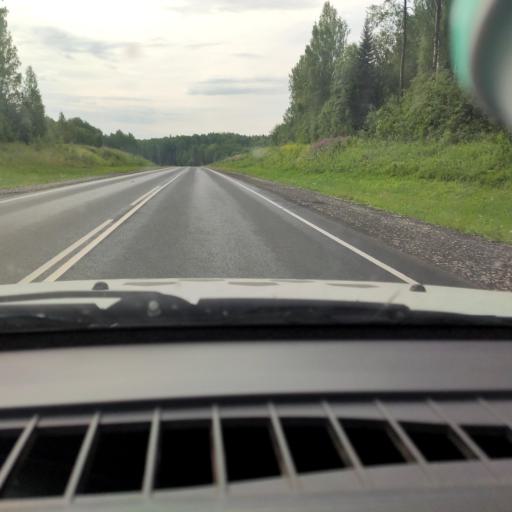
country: RU
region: Kirov
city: Kostino
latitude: 58.6575
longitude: 53.7705
